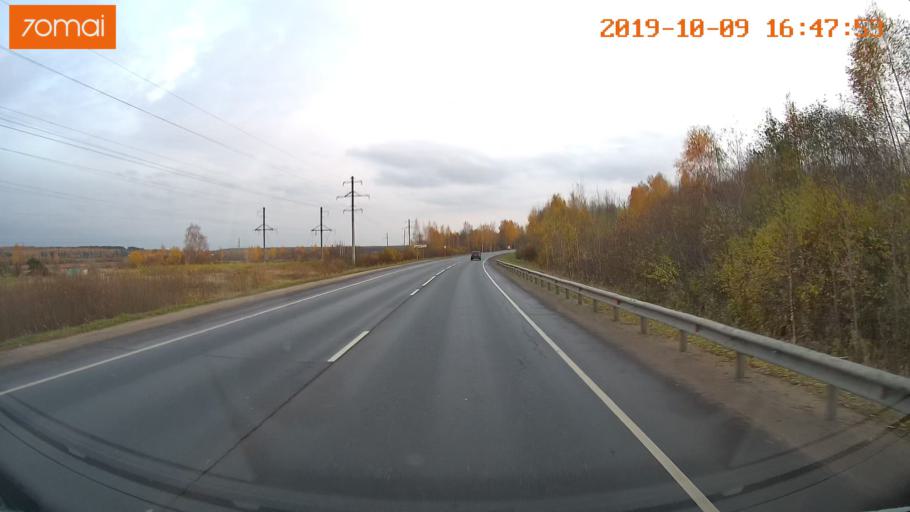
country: RU
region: Kostroma
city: Volgorechensk
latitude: 57.4337
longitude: 41.1844
